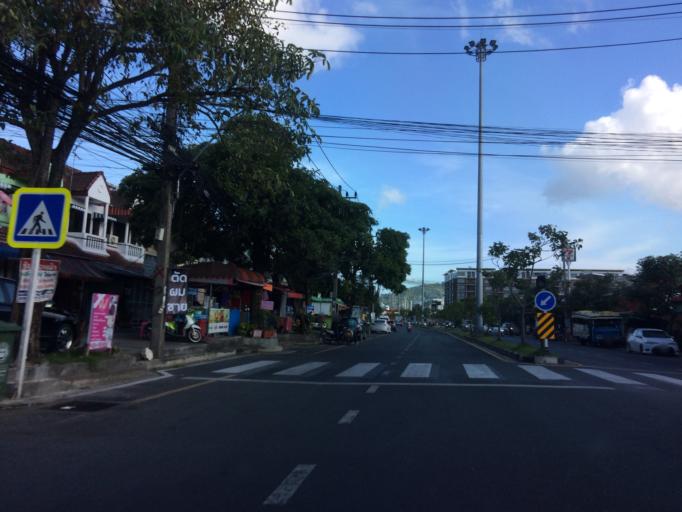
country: TH
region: Phuket
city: Kathu
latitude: 7.9127
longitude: 98.3468
